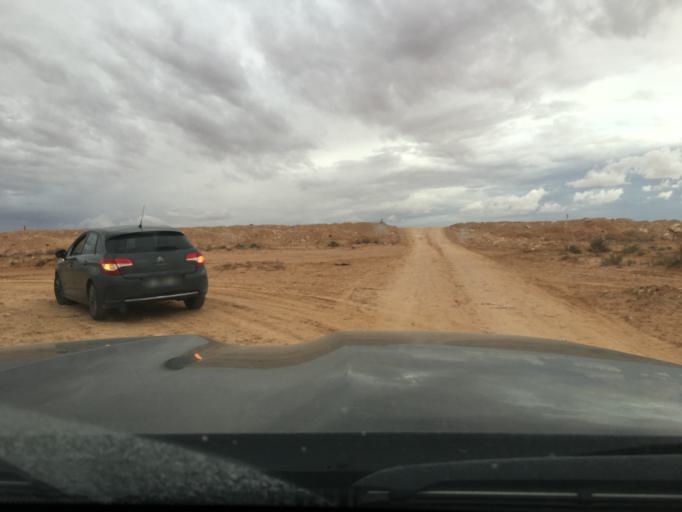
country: TN
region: Madanin
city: Medenine
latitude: 33.2594
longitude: 10.5736
